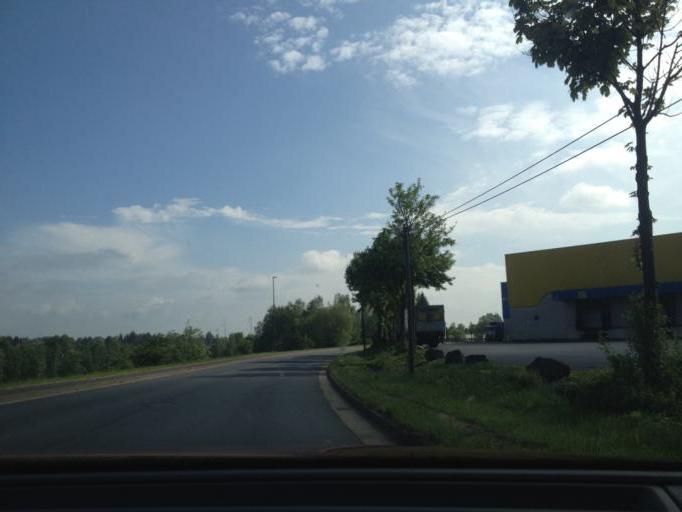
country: DE
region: Bavaria
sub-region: Upper Franconia
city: Marktredwitz
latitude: 50.0175
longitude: 12.0971
